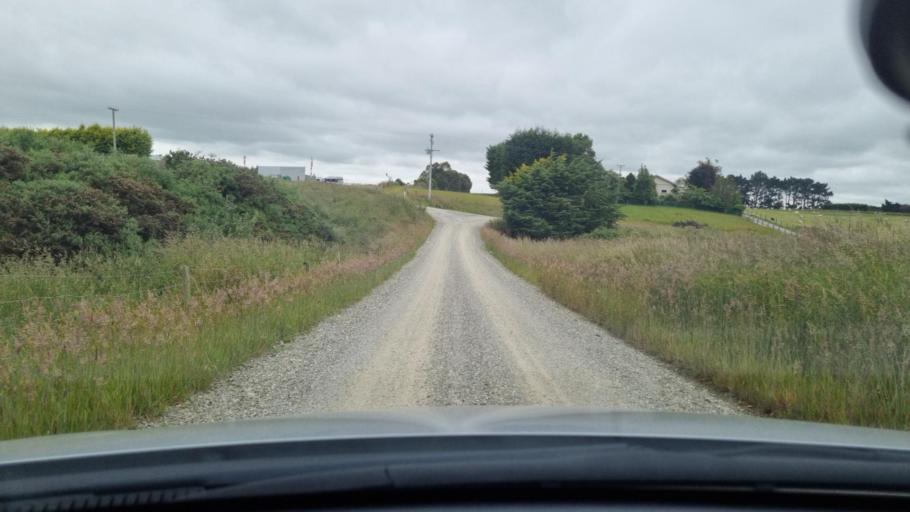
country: NZ
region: Southland
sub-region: Invercargill City
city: Invercargill
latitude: -46.3231
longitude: 168.3406
